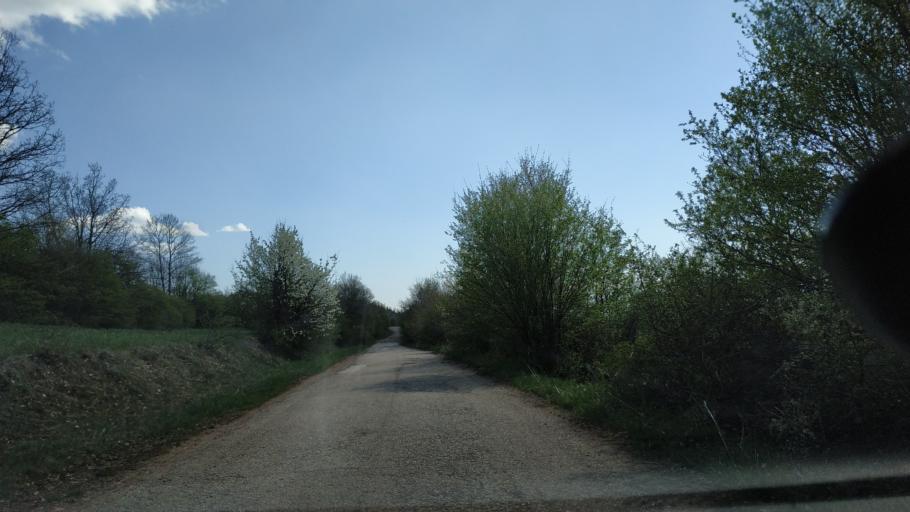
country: RS
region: Central Serbia
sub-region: Zajecarski Okrug
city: Soko Banja
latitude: 43.5626
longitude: 21.8946
